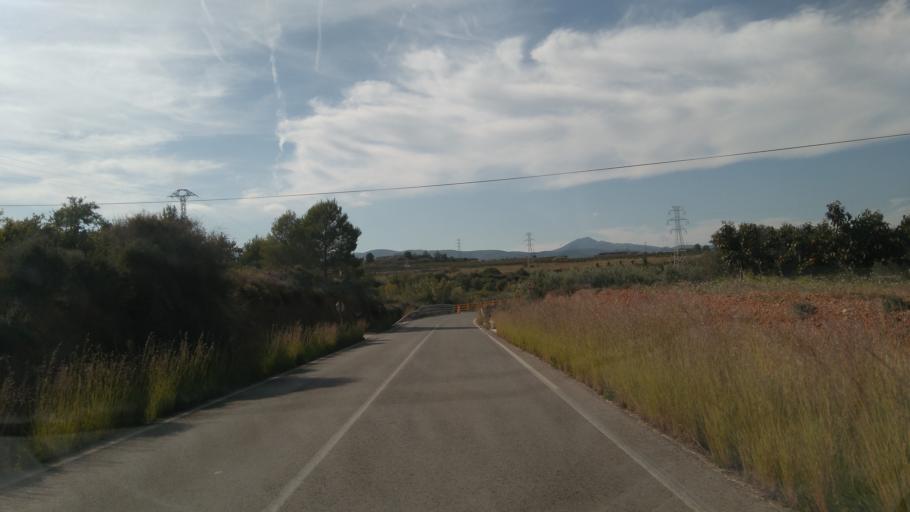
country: ES
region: Valencia
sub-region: Provincia de Valencia
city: Real de Montroi
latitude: 39.3295
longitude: -0.6003
